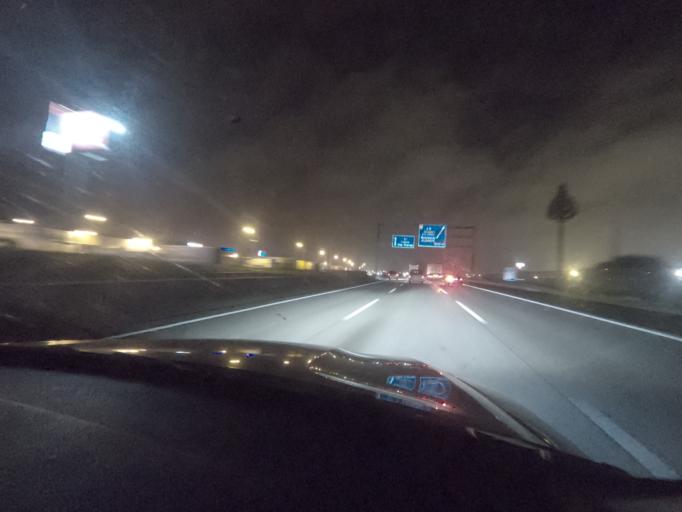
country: PT
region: Lisbon
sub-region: Alenquer
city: Carregado
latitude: 39.0340
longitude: -8.9597
